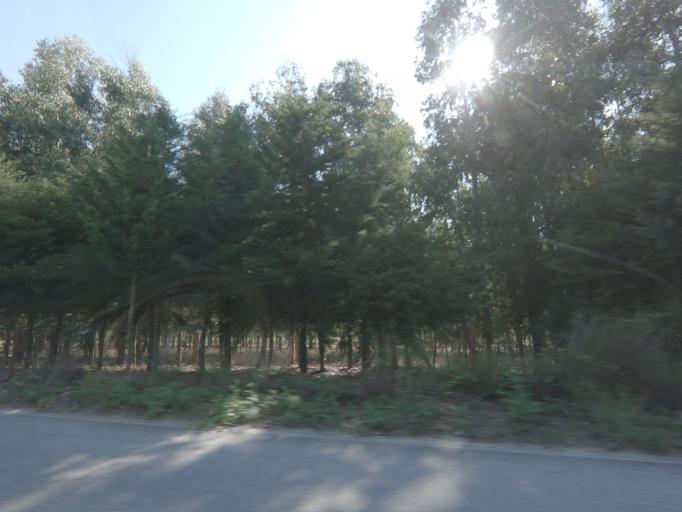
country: PT
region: Viseu
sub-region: Moimenta da Beira
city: Moimenta da Beira
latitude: 41.0371
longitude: -7.5689
